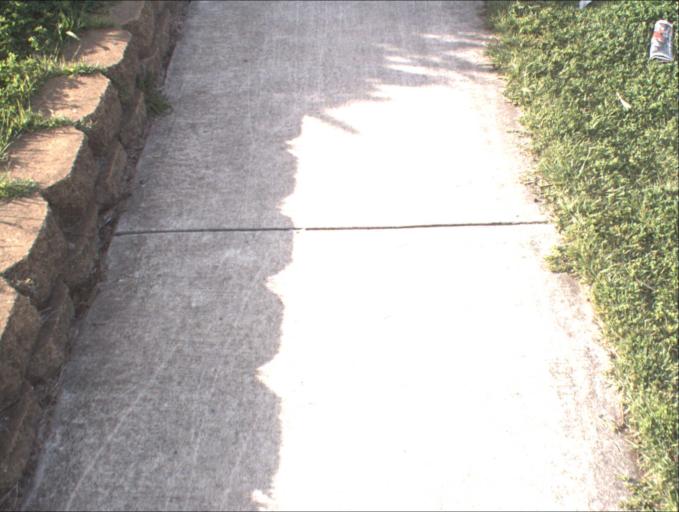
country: AU
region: Queensland
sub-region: Logan
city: Logan Reserve
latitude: -27.6989
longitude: 153.0944
